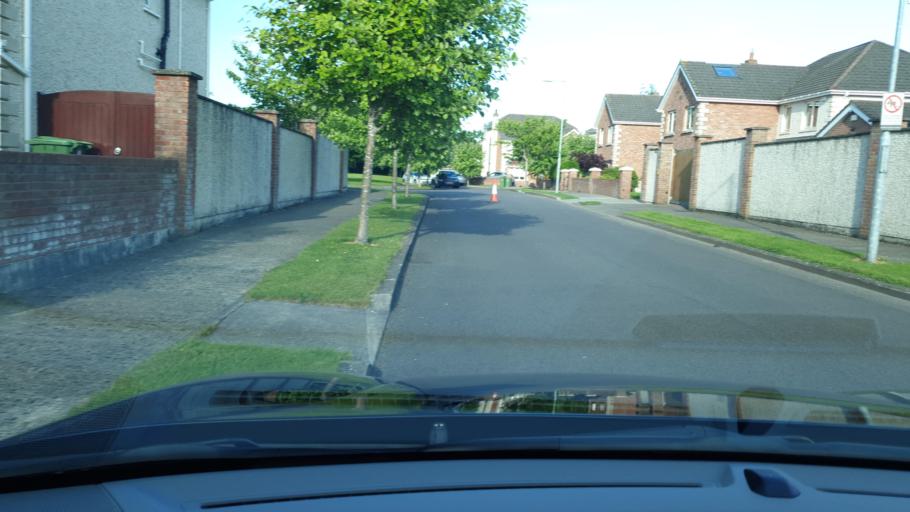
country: IE
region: Leinster
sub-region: An Mhi
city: Ashbourne
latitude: 53.5198
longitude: -6.4022
